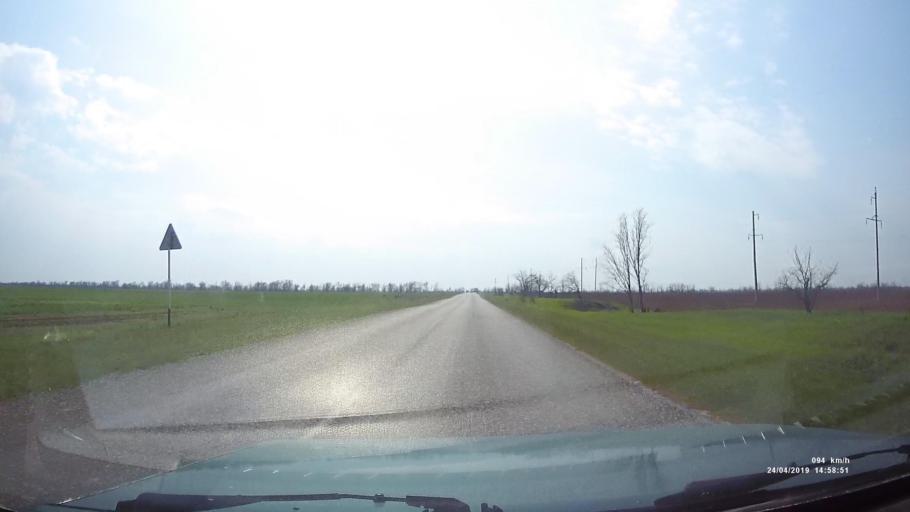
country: RU
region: Rostov
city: Remontnoye
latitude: 46.5674
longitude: 43.5895
